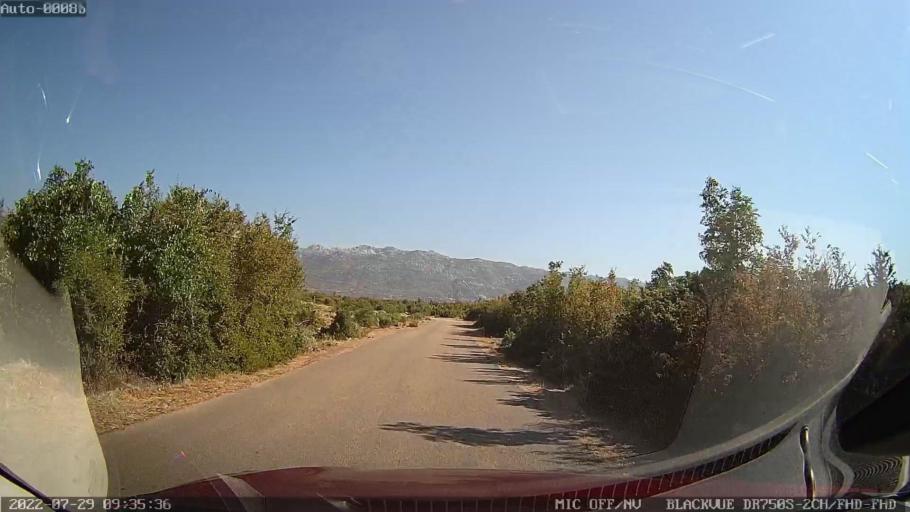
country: HR
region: Zadarska
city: Obrovac
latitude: 44.1870
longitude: 15.7325
